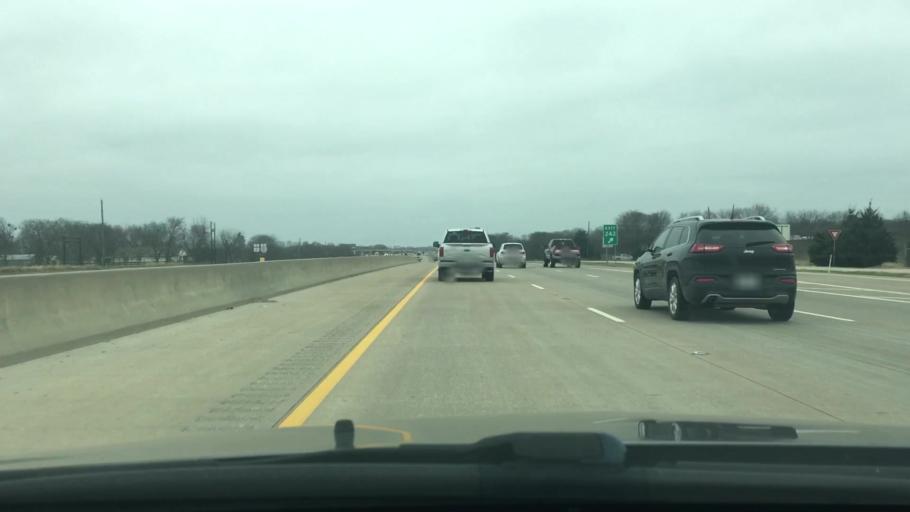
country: US
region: Texas
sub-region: Ellis County
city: Ennis
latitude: 32.2515
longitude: -96.5006
